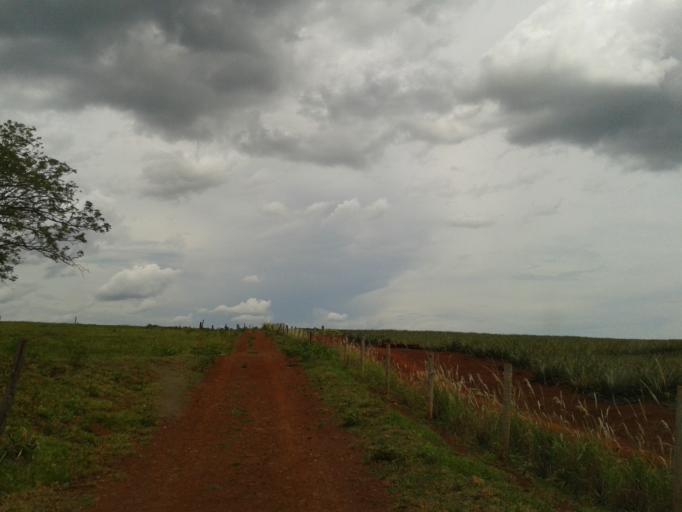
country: BR
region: Minas Gerais
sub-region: Centralina
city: Centralina
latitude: -18.6694
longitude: -49.2362
